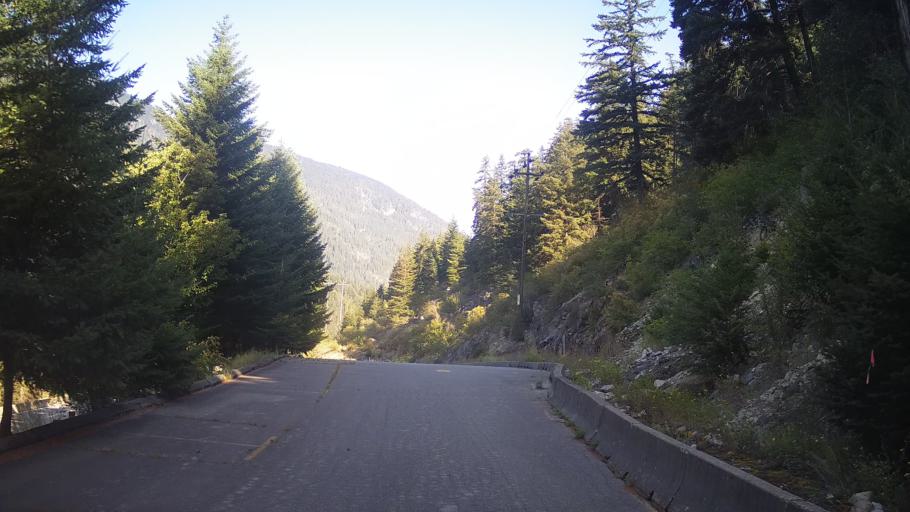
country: CA
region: British Columbia
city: Hope
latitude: 49.7796
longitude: -121.4434
